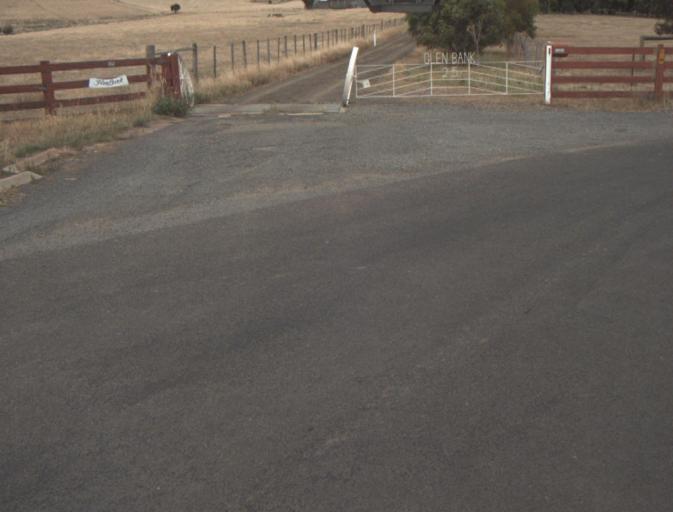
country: AU
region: Tasmania
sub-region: Northern Midlands
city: Evandale
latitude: -41.5068
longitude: 147.2544
